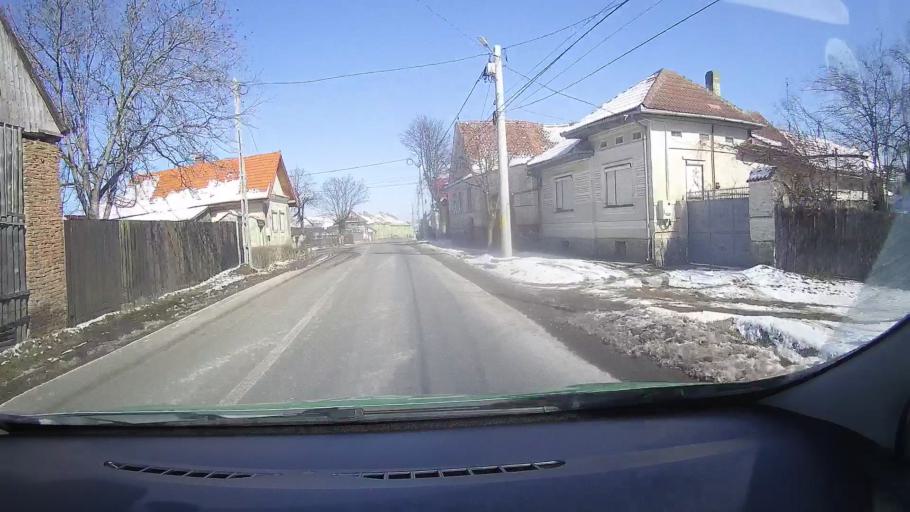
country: RO
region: Brasov
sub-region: Comuna Parau
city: Parau
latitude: 45.8730
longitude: 25.2079
